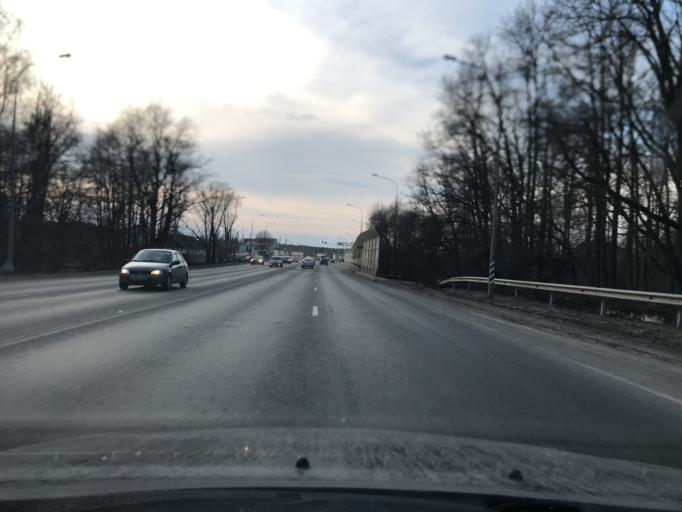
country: RU
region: Kaluga
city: Mstikhino
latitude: 54.5563
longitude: 36.1297
